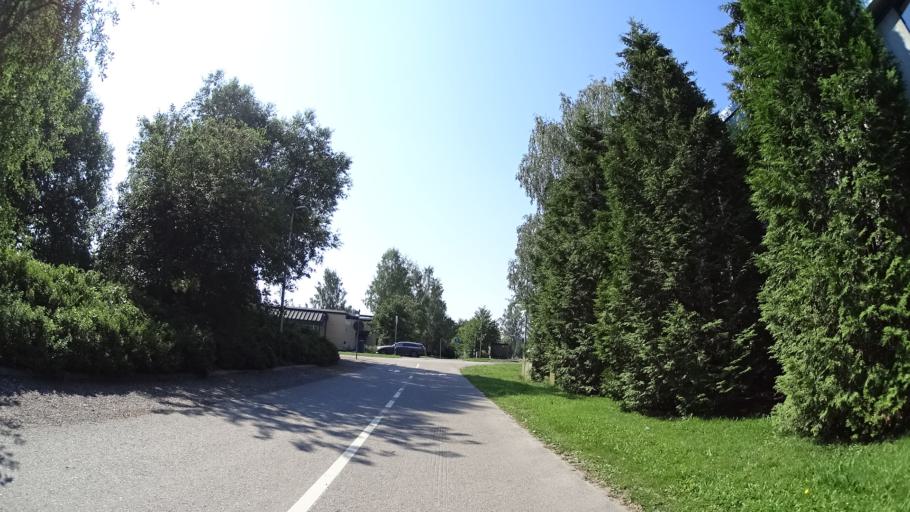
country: FI
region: Uusimaa
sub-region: Helsinki
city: Kerava
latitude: 60.3811
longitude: 25.0930
